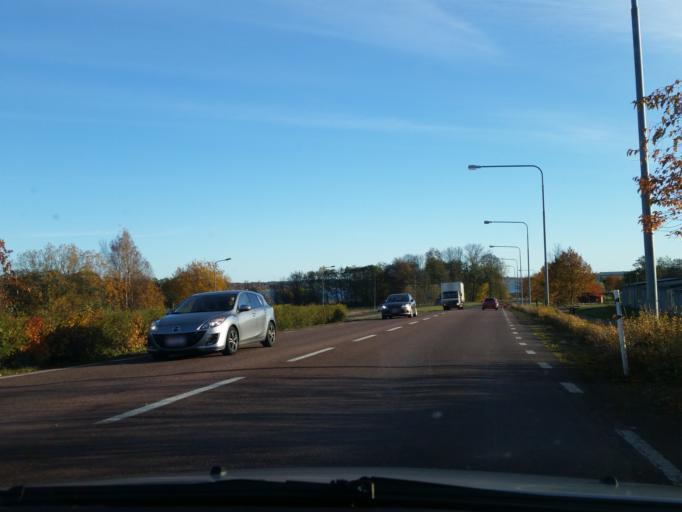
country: AX
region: Mariehamns stad
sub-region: Mariehamn
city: Mariehamn
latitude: 60.1138
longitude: 19.9402
